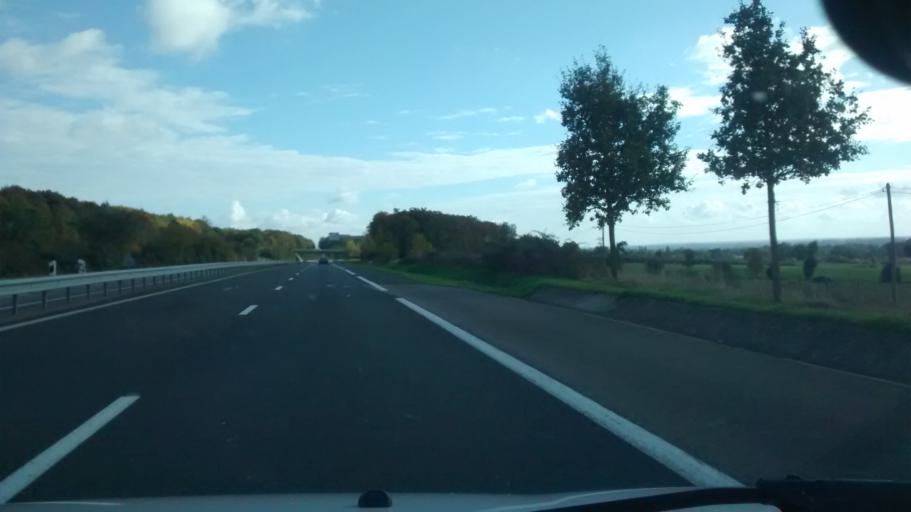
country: FR
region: Pays de la Loire
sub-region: Departement de Maine-et-Loire
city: Combree
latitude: 47.7166
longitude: -1.0187
